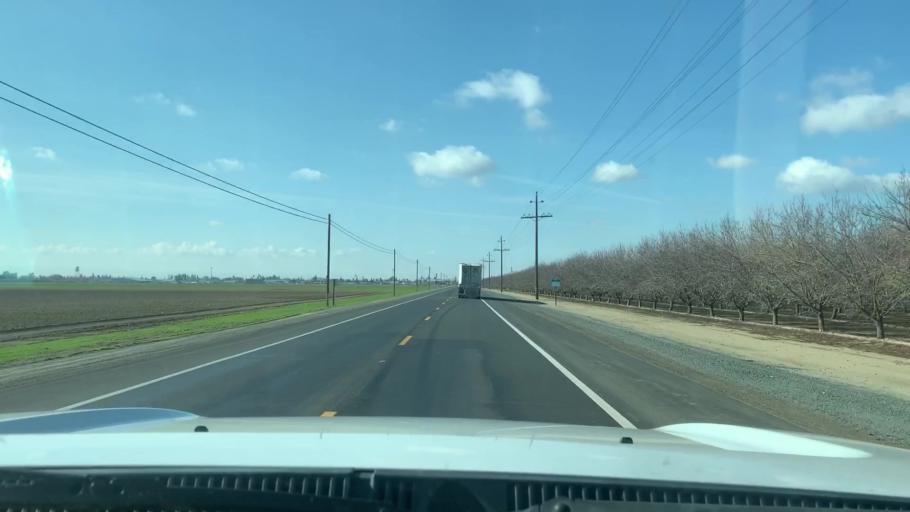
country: US
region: California
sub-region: Kern County
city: Wasco
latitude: 35.6016
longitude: -119.3138
